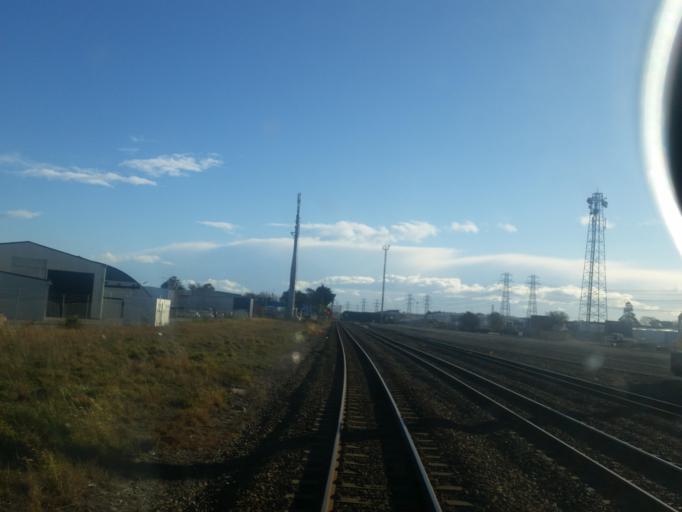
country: NZ
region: Canterbury
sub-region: Christchurch City
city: Christchurch
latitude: -43.5412
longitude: 172.5824
